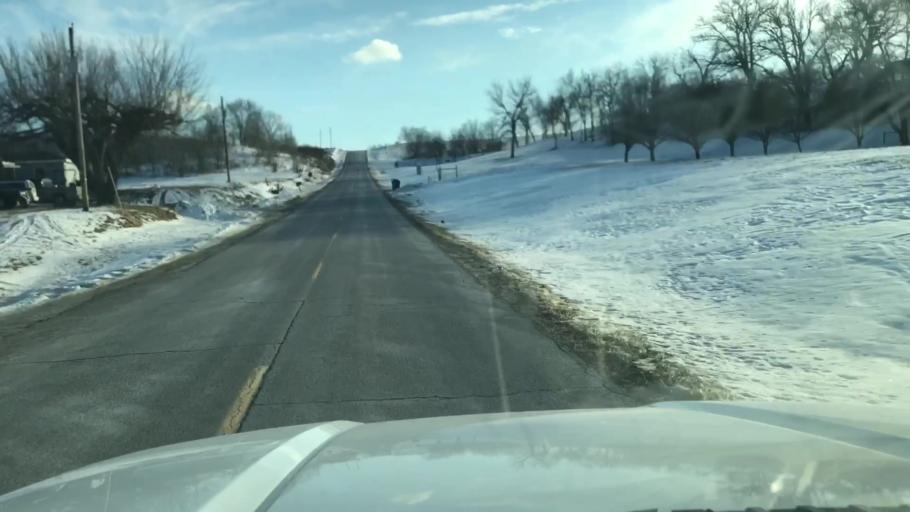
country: US
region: Missouri
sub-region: Holt County
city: Oregon
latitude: 40.0723
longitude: -94.9747
